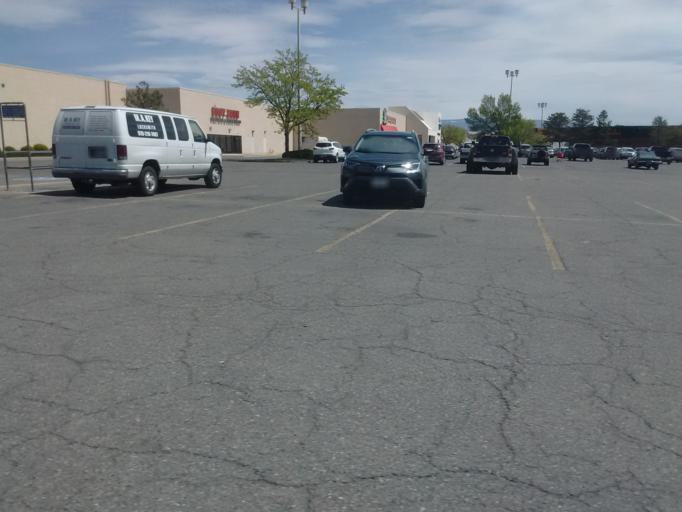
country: US
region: Colorado
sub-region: Mesa County
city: Redlands
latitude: 39.0918
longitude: -108.6049
